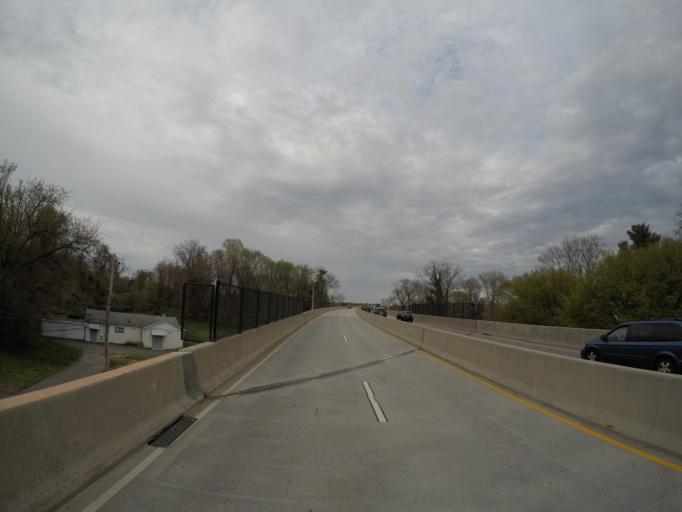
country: US
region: Maryland
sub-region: Harford County
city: Havre de Grace
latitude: 39.5568
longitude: -76.0988
